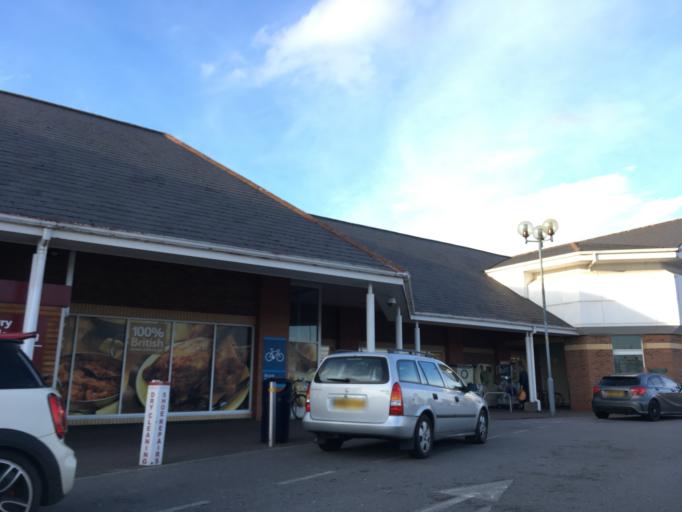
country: GB
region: England
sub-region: Borough of Stockport
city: Cheadle Hulme
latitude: 53.3498
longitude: -2.2051
